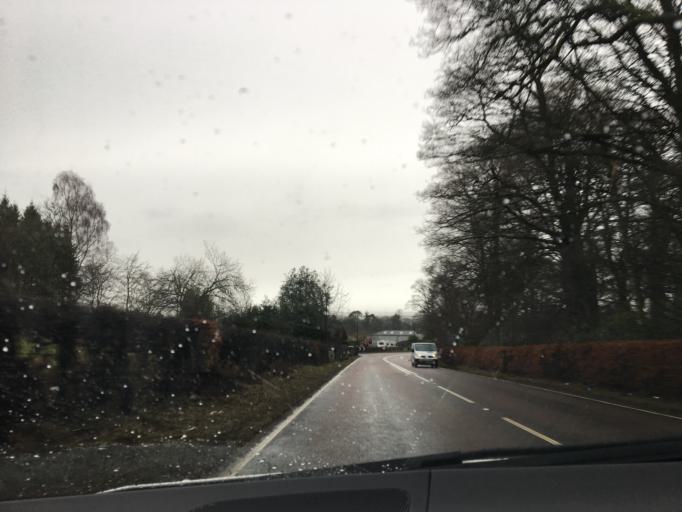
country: GB
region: Scotland
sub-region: Stirling
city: Doune
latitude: 56.1807
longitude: -4.0646
